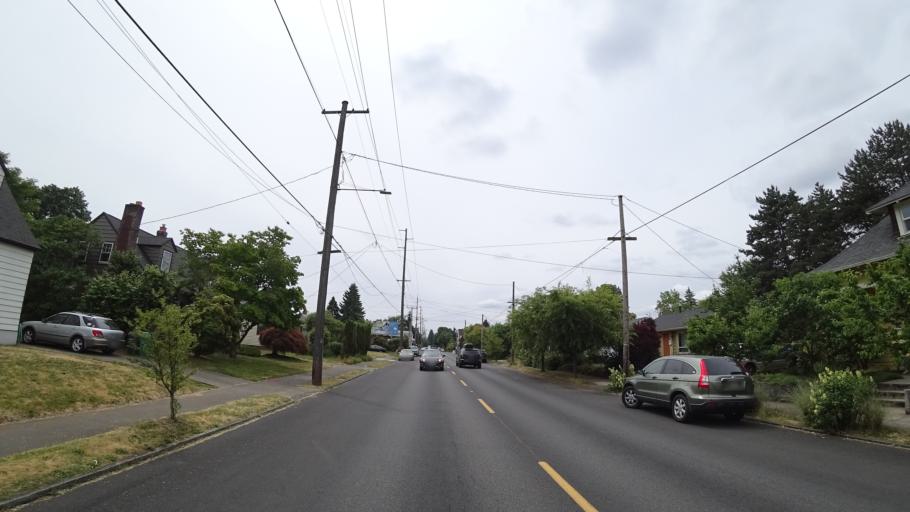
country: US
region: Oregon
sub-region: Multnomah County
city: Portland
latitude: 45.5674
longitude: -122.6956
